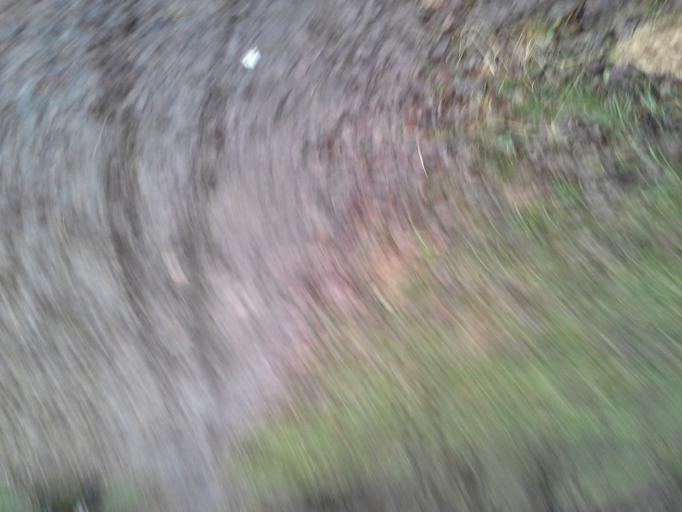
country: RU
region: Moscow
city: Tyoply Stan
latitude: 55.5954
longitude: 37.4966
